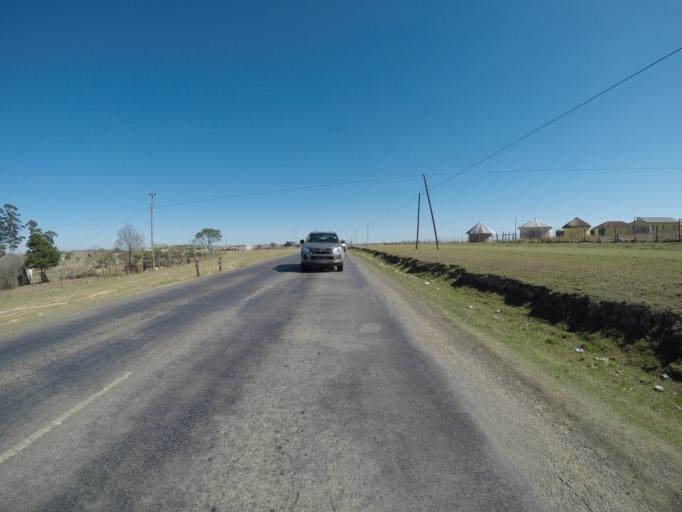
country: ZA
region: Eastern Cape
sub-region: OR Tambo District Municipality
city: Mthatha
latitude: -31.7880
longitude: 28.7433
